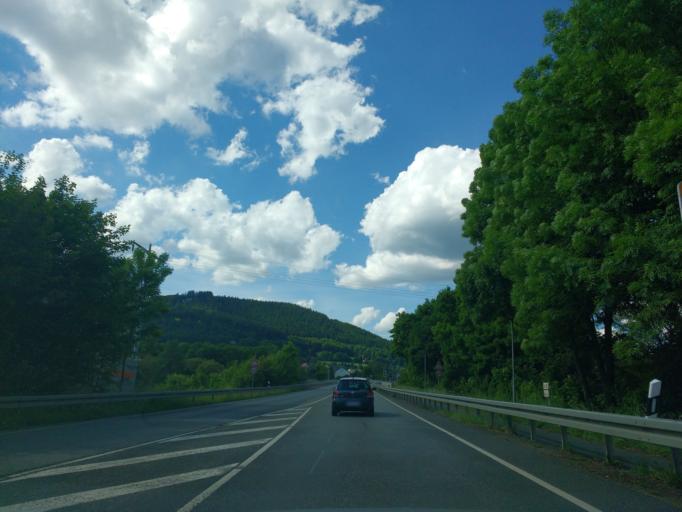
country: DE
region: Hesse
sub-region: Regierungsbezirk Giessen
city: Breidenbach
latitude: 50.9186
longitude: 8.4681
